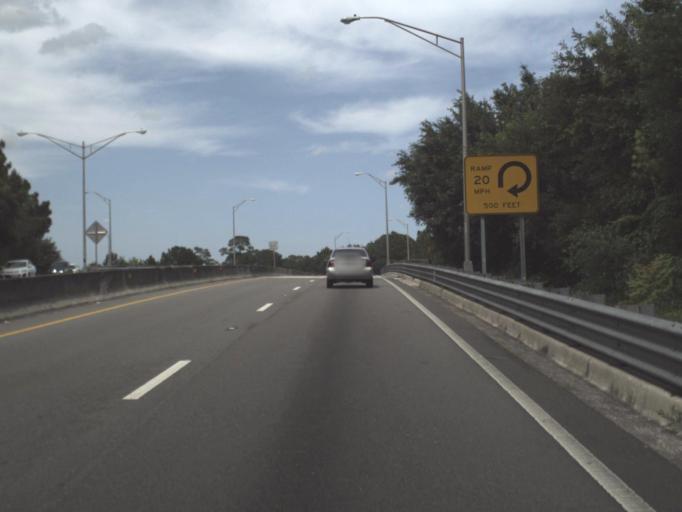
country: US
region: Florida
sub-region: Duval County
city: Jacksonville
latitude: 30.2950
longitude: -81.7213
